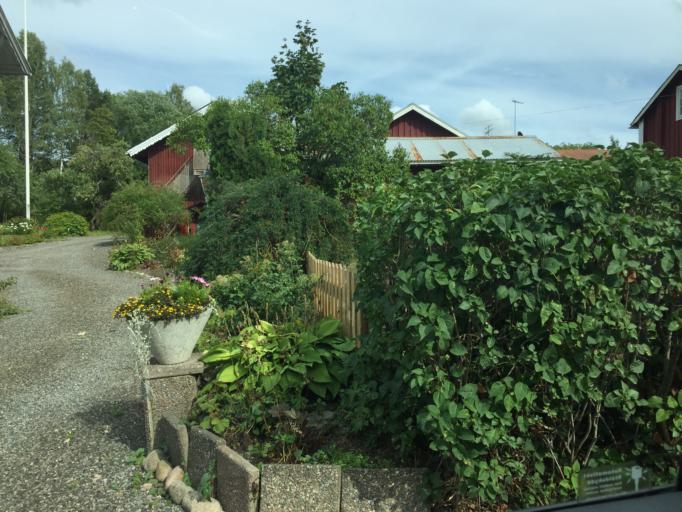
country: SE
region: OErebro
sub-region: Hallefors Kommun
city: Haellefors
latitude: 59.7066
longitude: 14.5365
